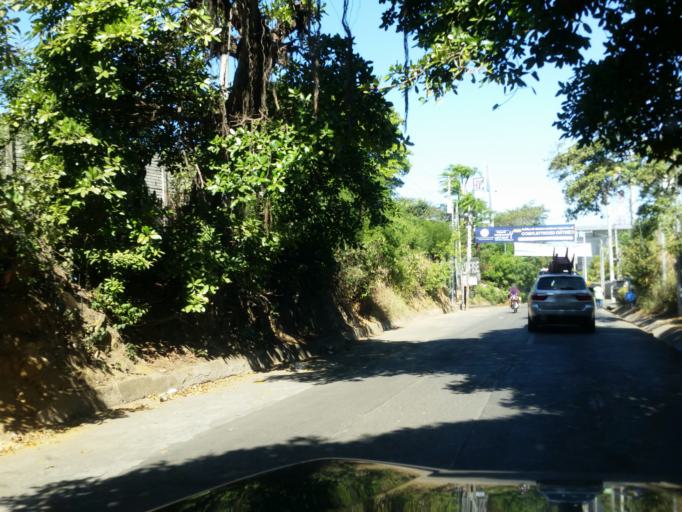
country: NI
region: Managua
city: Managua
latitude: 12.1014
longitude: -86.2499
